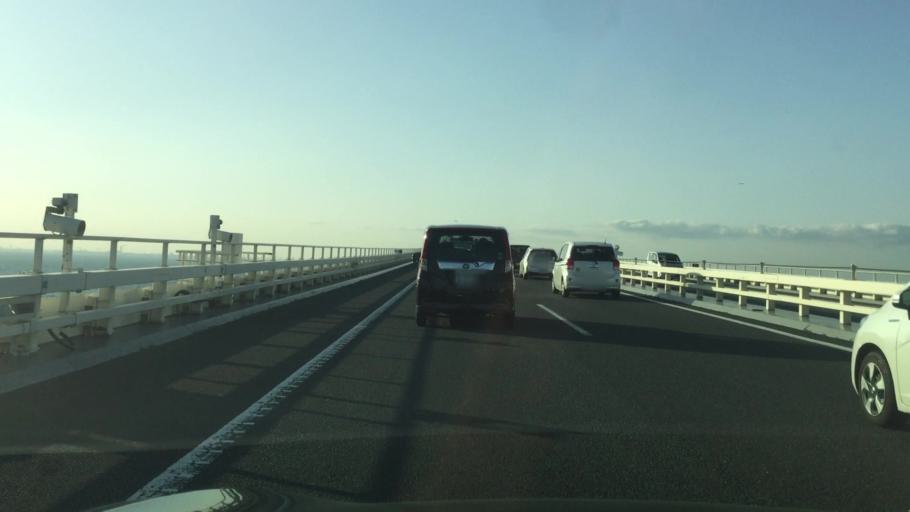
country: JP
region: Chiba
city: Kisarazu
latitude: 35.4505
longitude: 139.8947
